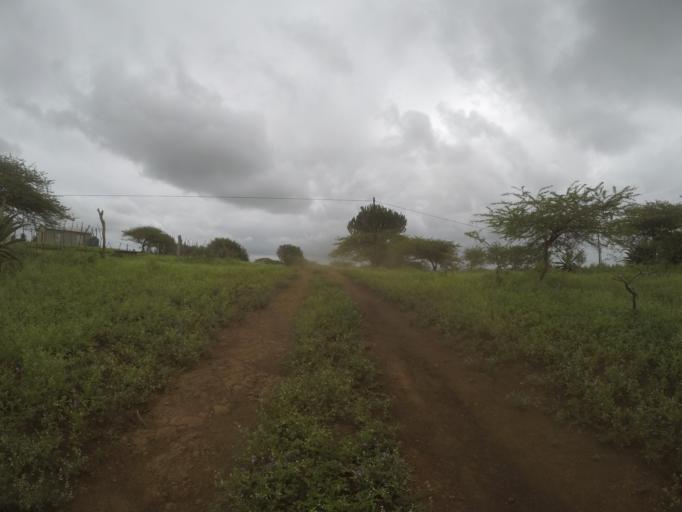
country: ZA
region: KwaZulu-Natal
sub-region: uThungulu District Municipality
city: Empangeni
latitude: -28.5998
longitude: 31.8510
